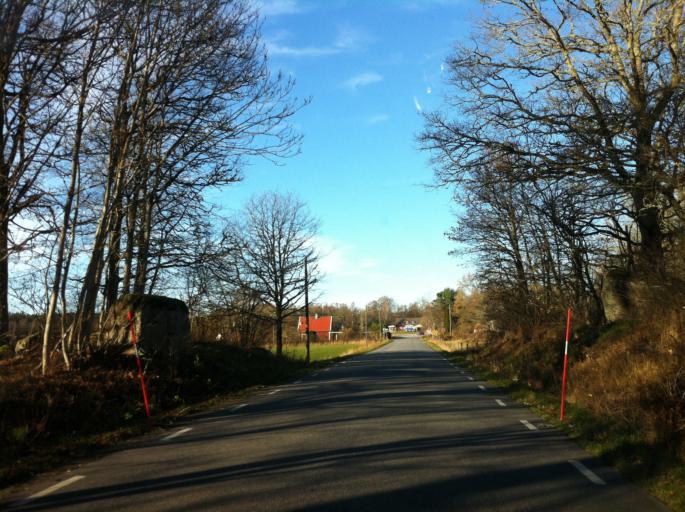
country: SE
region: Blekinge
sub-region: Ronneby Kommun
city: Brakne-Hoby
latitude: 56.2052
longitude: 15.0962
